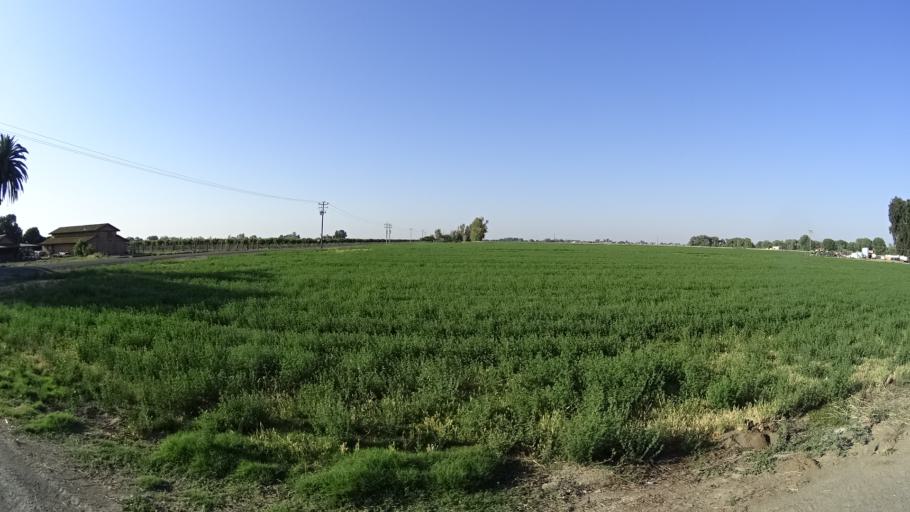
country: US
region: California
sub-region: Kings County
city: Lemoore
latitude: 36.2549
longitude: -119.7451
